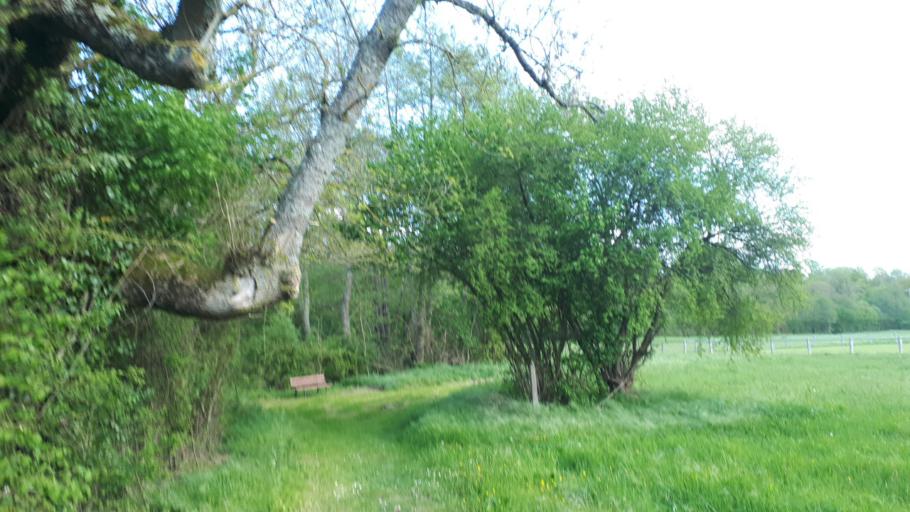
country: FR
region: Centre
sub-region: Departement du Loir-et-Cher
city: Aze
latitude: 47.8491
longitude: 0.9974
